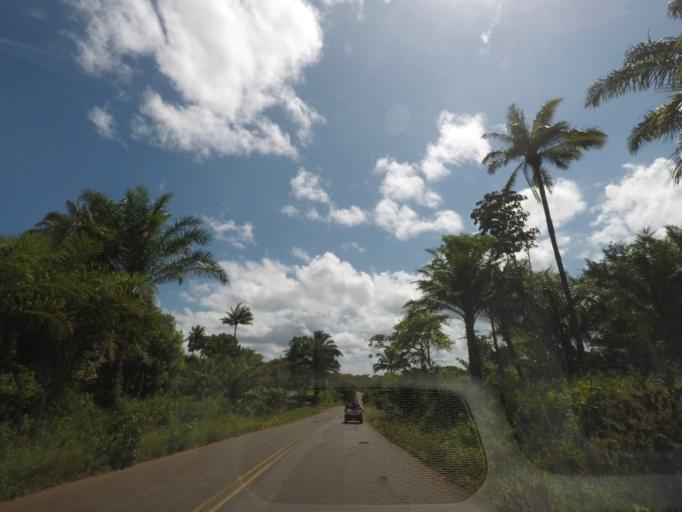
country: BR
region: Bahia
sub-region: Taperoa
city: Taperoa
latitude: -13.5220
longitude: -39.1015
